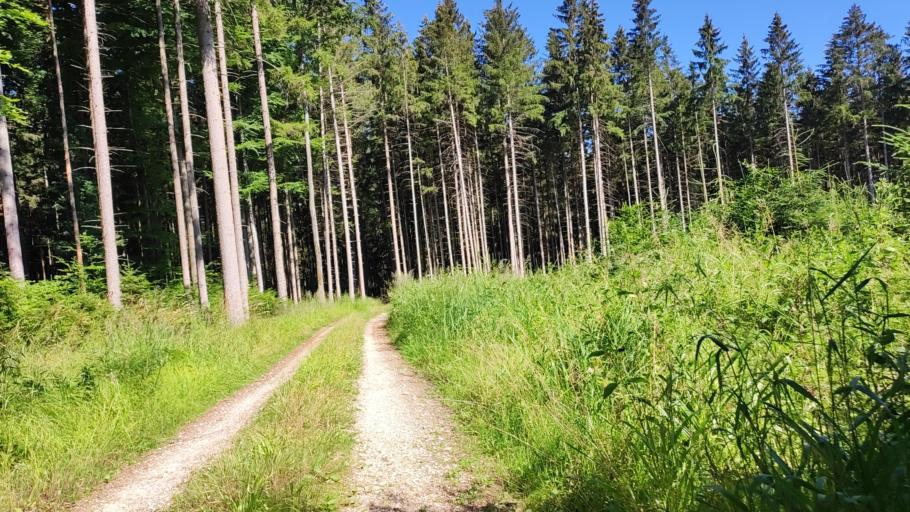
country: DE
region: Bavaria
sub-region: Swabia
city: Landensberg
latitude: 48.4664
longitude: 10.5286
